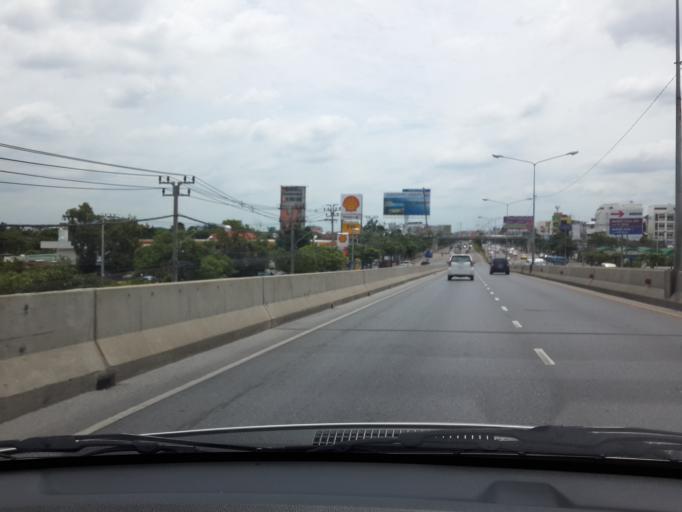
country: TH
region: Bangkok
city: Min Buri
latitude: 13.8004
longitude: 100.7170
